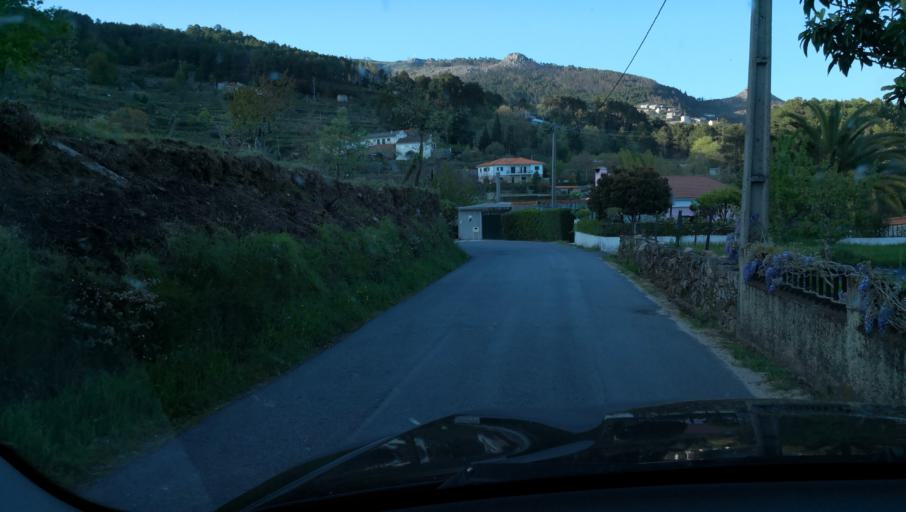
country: PT
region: Vila Real
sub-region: Vila Real
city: Vila Real
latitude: 41.3211
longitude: -7.7788
